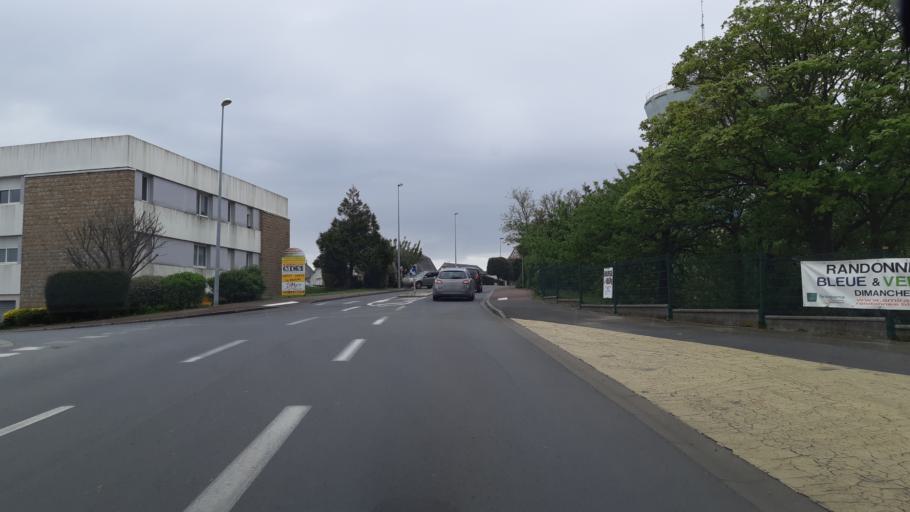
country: FR
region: Lower Normandy
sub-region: Departement de la Manche
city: Donville-les-Bains
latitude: 48.8532
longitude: -1.5637
